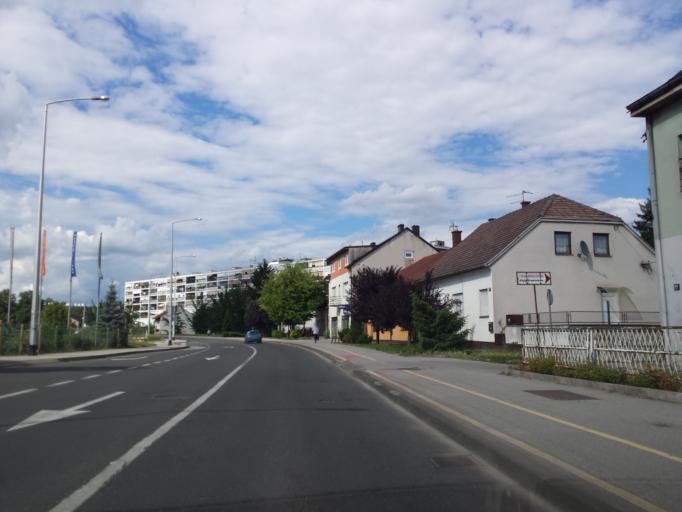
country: HR
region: Grad Zagreb
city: Novi Zagreb
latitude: 45.7731
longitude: 15.9525
